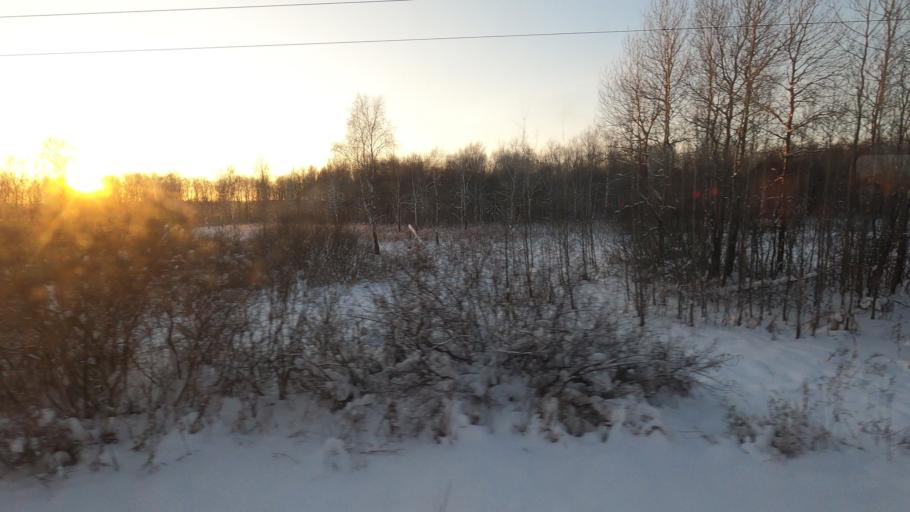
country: RU
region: Moskovskaya
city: Dmitrov
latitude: 56.3696
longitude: 37.5257
